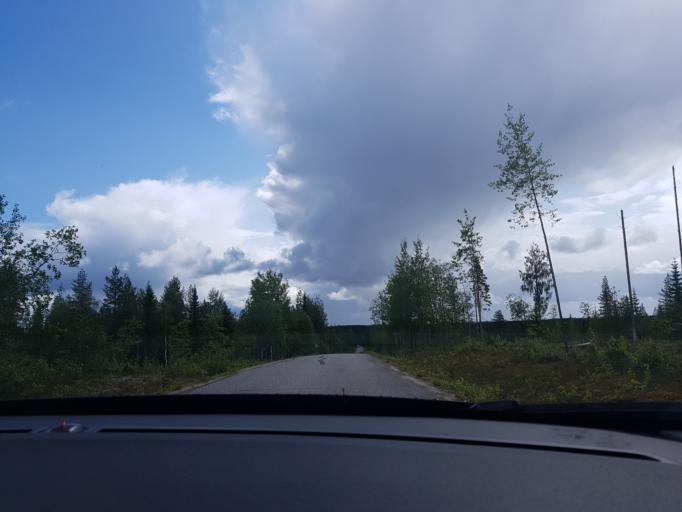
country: FI
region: Kainuu
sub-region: Kehys-Kainuu
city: Kuhmo
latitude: 64.4566
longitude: 29.6491
